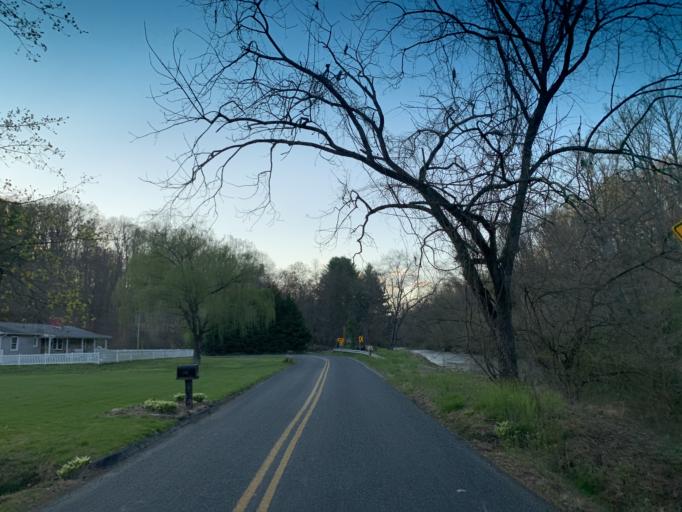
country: US
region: Maryland
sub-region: Harford County
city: Bel Air North
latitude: 39.6259
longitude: -76.3446
